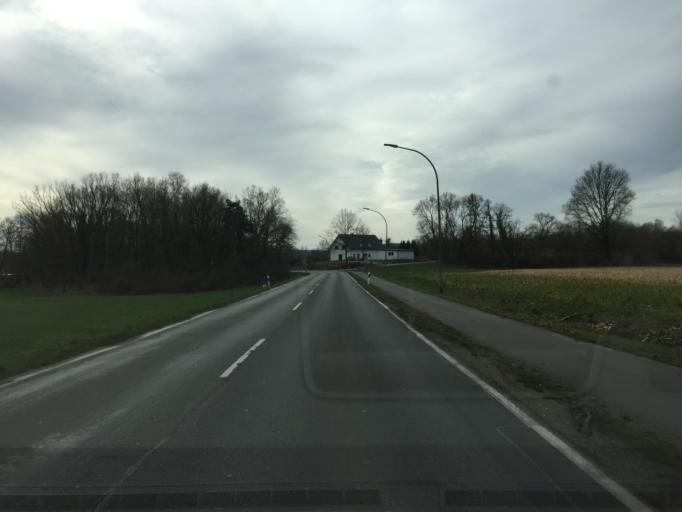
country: DE
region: North Rhine-Westphalia
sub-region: Regierungsbezirk Detmold
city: Lage
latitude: 51.9694
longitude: 8.8011
